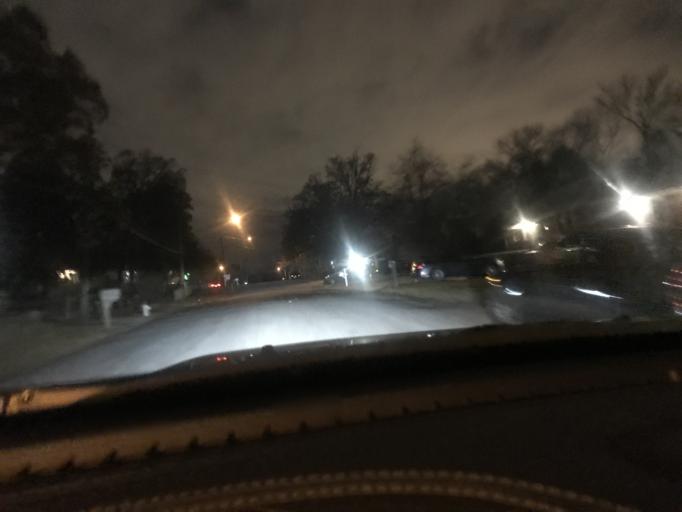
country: US
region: Maryland
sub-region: Prince George's County
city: Temple Hills
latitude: 38.8119
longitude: -76.9643
